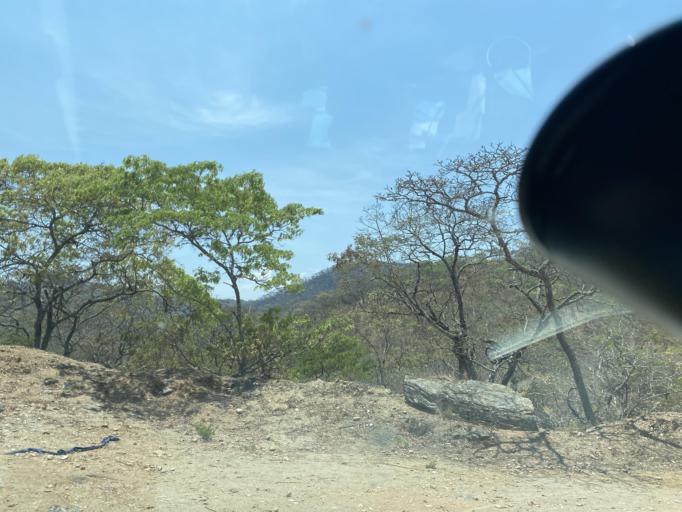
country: ZM
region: Lusaka
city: Kafue
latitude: -15.8043
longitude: 28.4249
